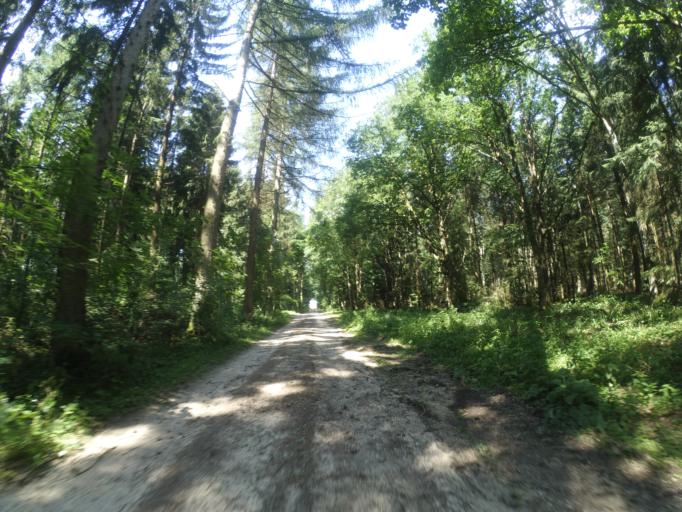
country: DE
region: Baden-Wuerttemberg
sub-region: Tuebingen Region
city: Dornstadt
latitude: 48.4554
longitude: 9.8742
